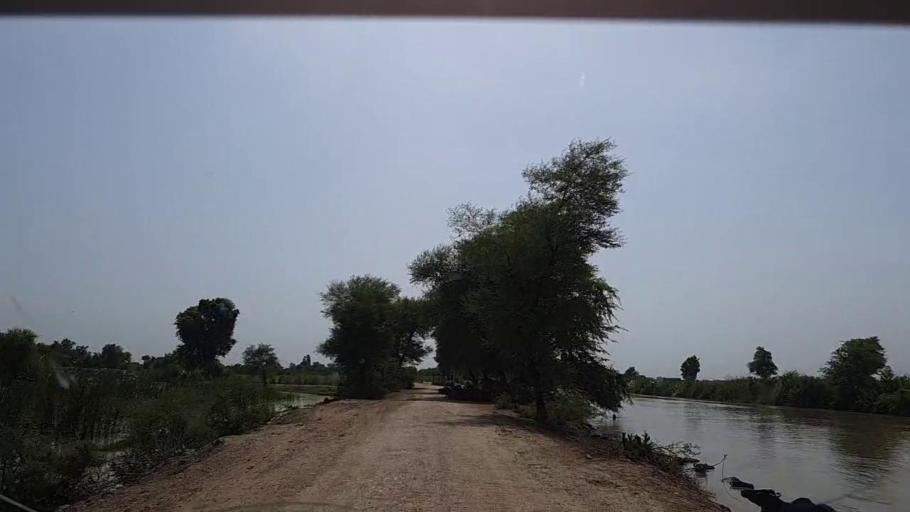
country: PK
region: Sindh
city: Ghotki
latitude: 28.0782
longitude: 69.3897
